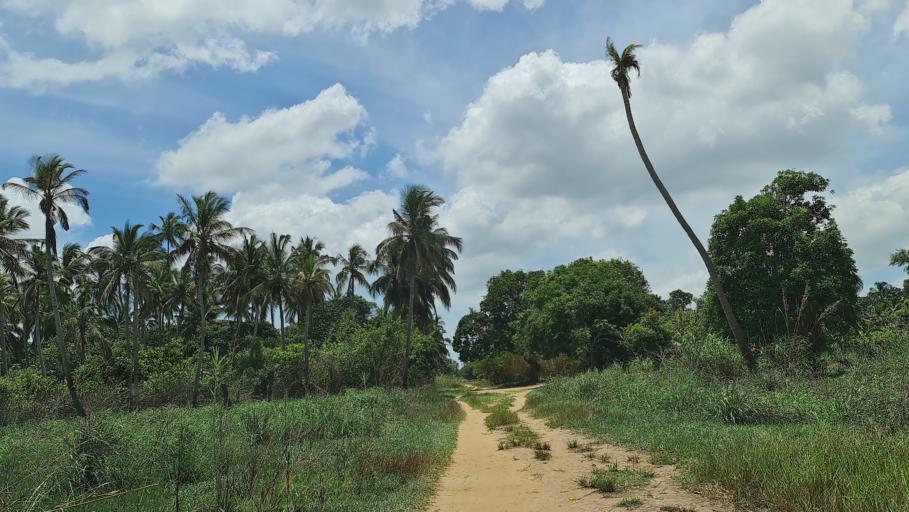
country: MZ
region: Zambezia
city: Quelimane
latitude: -17.5759
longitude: 37.3742
